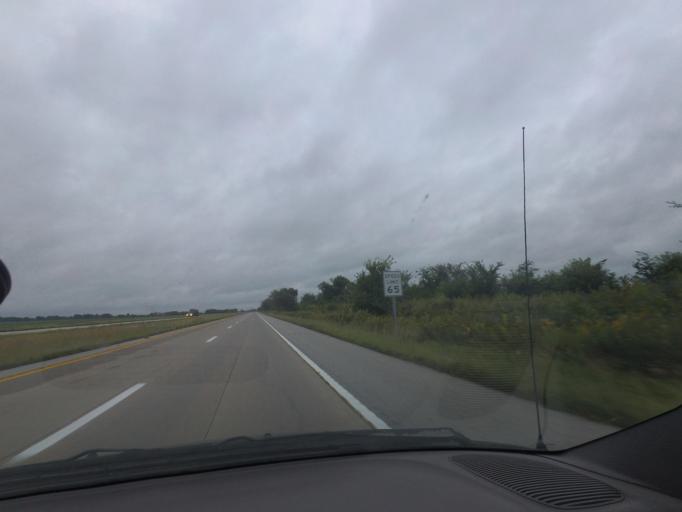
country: US
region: Missouri
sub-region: Marion County
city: Monroe City
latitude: 39.6613
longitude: -91.8266
